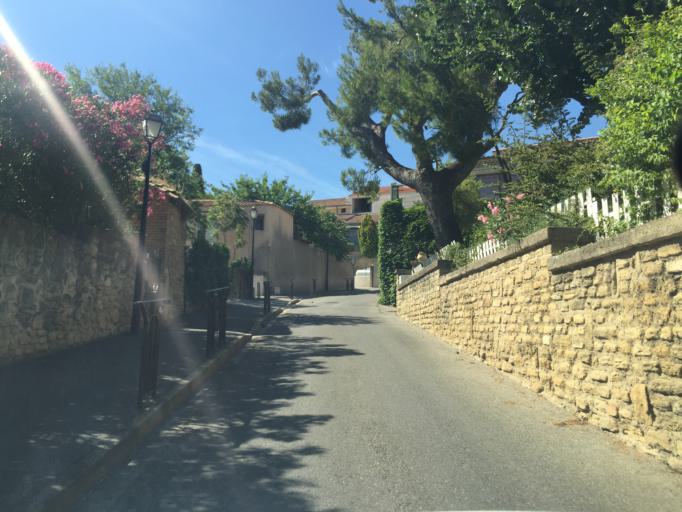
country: FR
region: Provence-Alpes-Cote d'Azur
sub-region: Departement du Vaucluse
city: Chateauneuf-du-Pape
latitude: 44.0549
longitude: 4.8323
